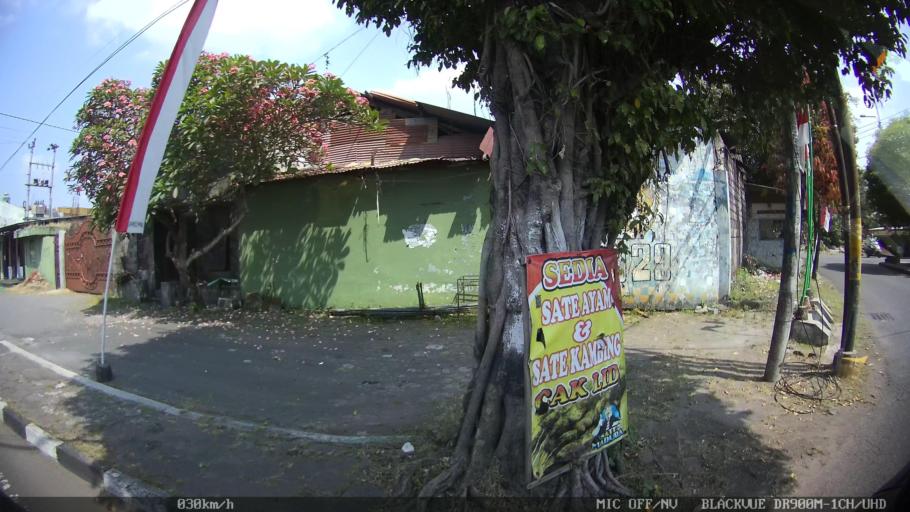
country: ID
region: Daerah Istimewa Yogyakarta
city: Yogyakarta
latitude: -7.8132
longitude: 110.3919
